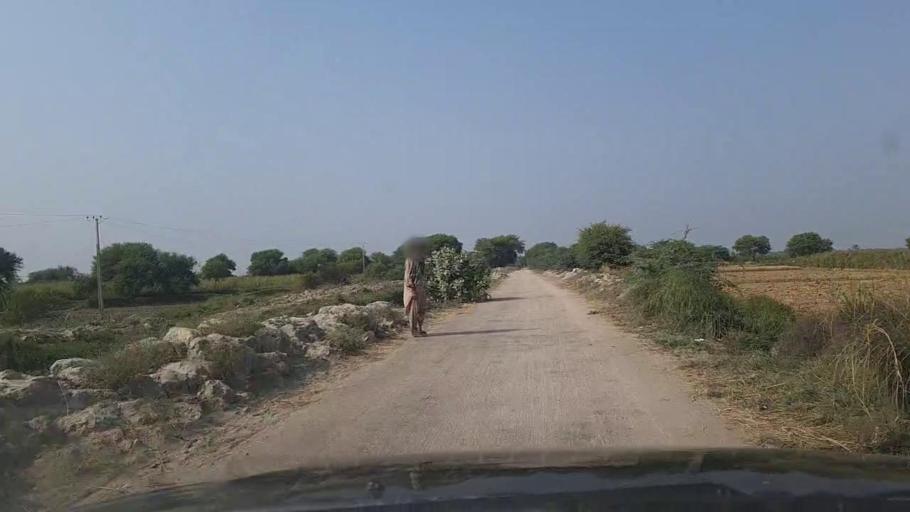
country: PK
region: Sindh
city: Mirpur Batoro
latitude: 24.7019
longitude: 68.2561
